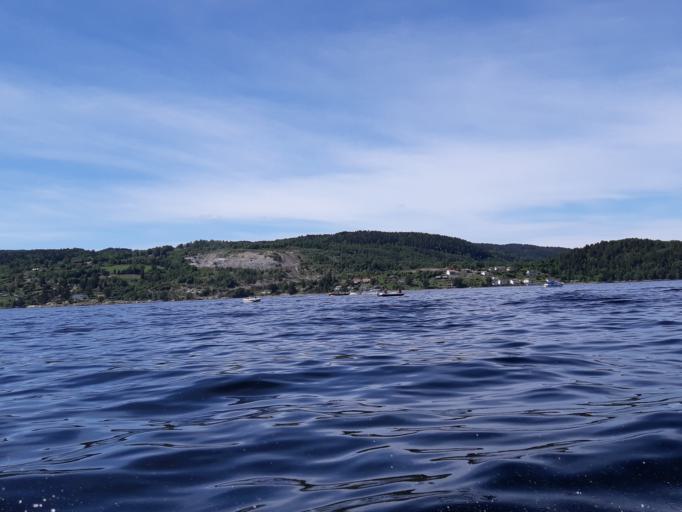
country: NO
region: Akershus
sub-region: Frogn
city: Drobak
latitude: 59.6642
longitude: 10.6233
